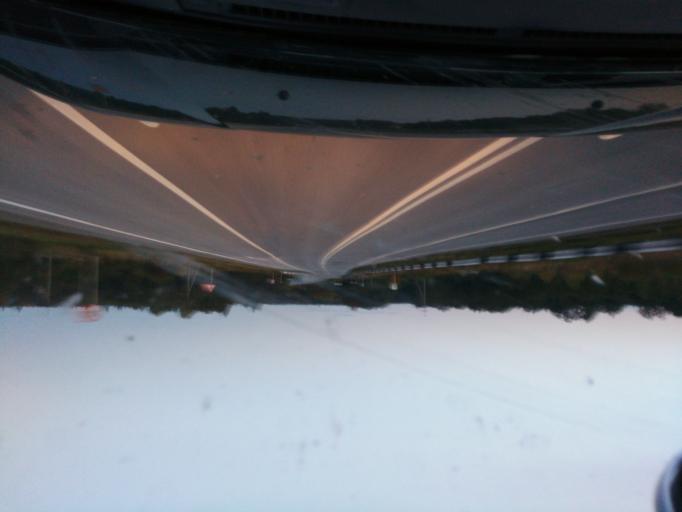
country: RU
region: Perm
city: Verkhnechusovskiye Gorodki
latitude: 58.2657
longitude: 57.3426
